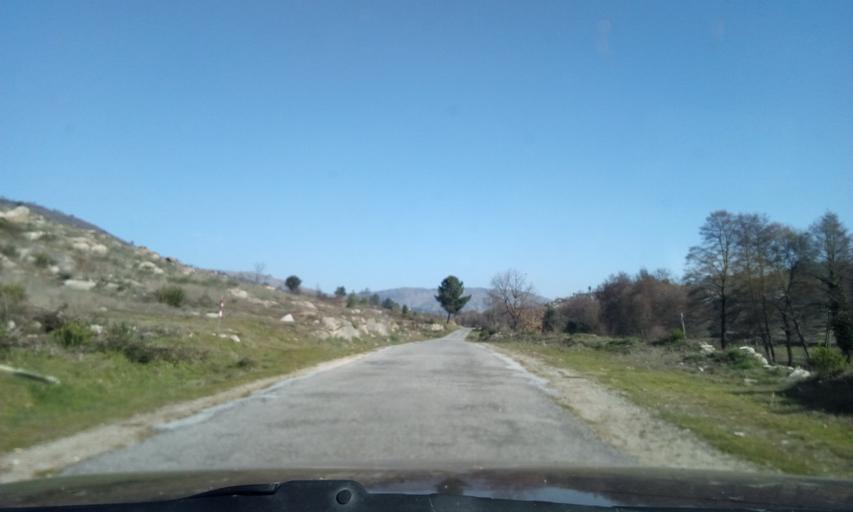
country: PT
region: Guarda
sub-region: Celorico da Beira
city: Celorico da Beira
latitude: 40.6746
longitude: -7.4565
